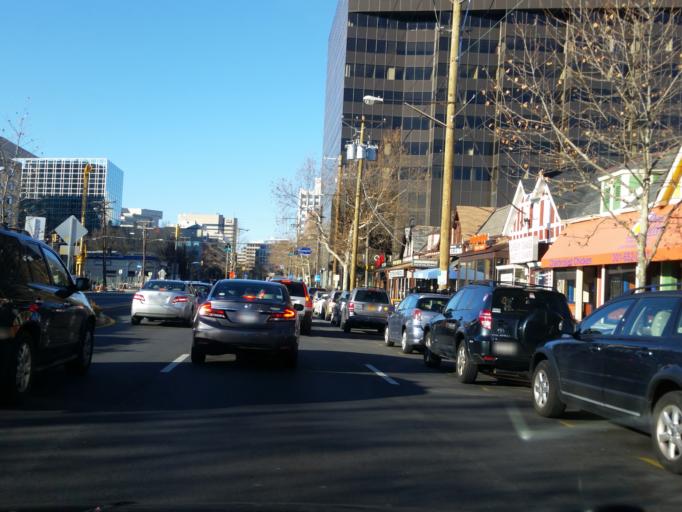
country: US
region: Maryland
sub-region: Montgomery County
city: Bethesda
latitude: 38.9795
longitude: -77.0918
